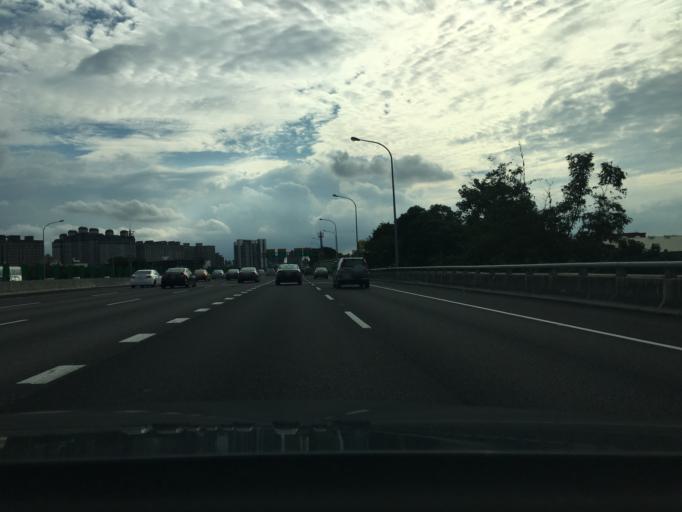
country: TW
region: Taiwan
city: Taoyuan City
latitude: 24.9714
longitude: 121.2178
